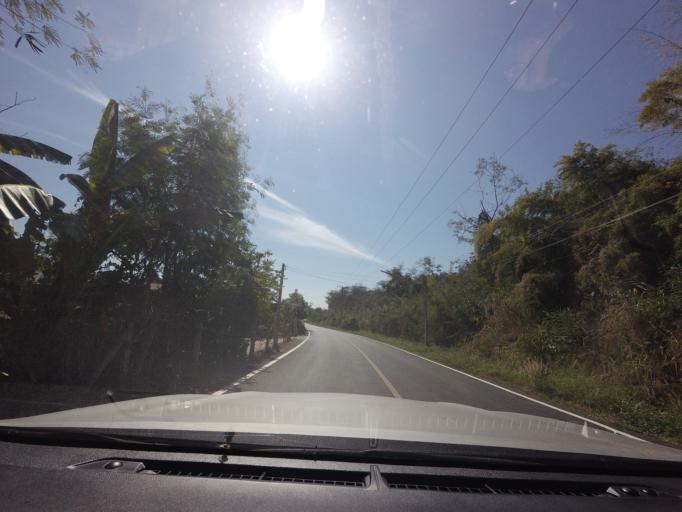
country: TH
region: Chiang Mai
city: Pai
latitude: 19.3713
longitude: 98.4347
